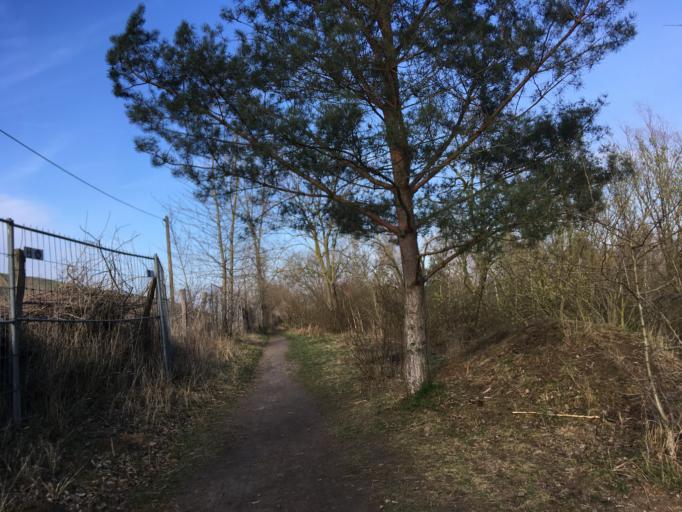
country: DE
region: Berlin
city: Blankenfelde
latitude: 52.6355
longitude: 13.4067
